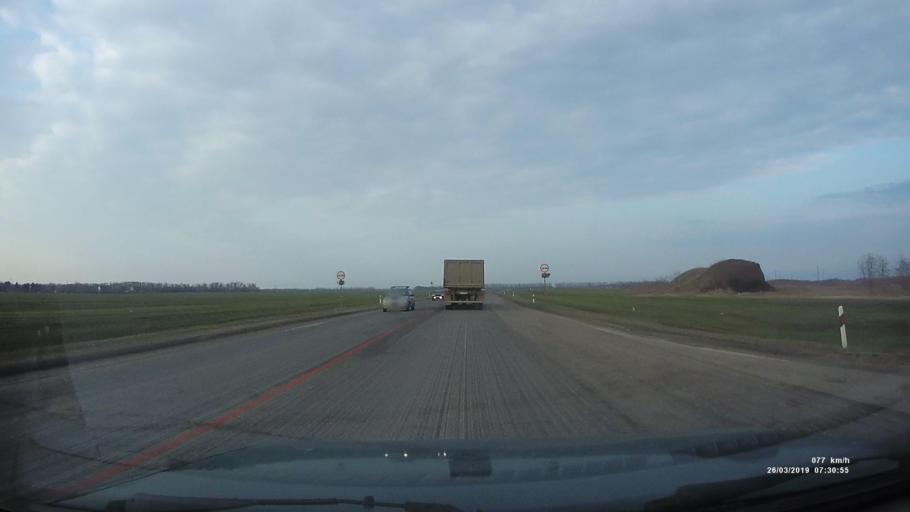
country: RU
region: Rostov
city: Novobessergenovka
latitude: 47.2345
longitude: 38.7996
